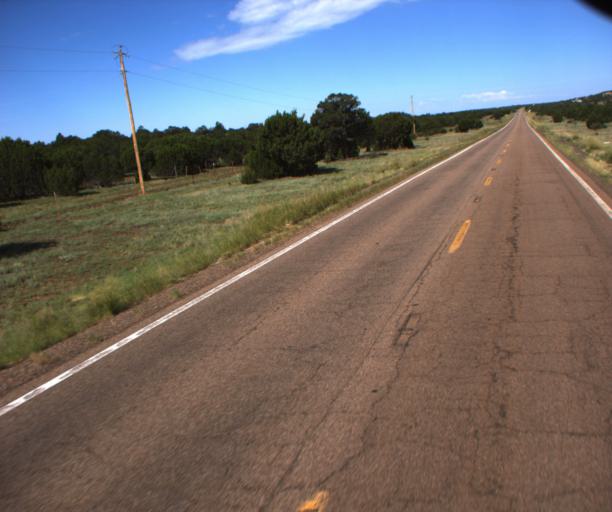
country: US
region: Arizona
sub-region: Navajo County
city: Pinetop-Lakeside
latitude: 34.2742
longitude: -109.7687
